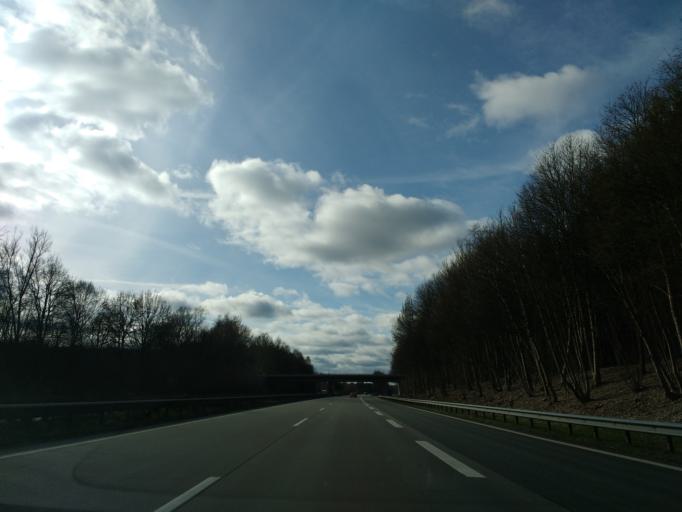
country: DE
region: Lower Saxony
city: Langen
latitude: 53.6124
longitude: 8.6613
